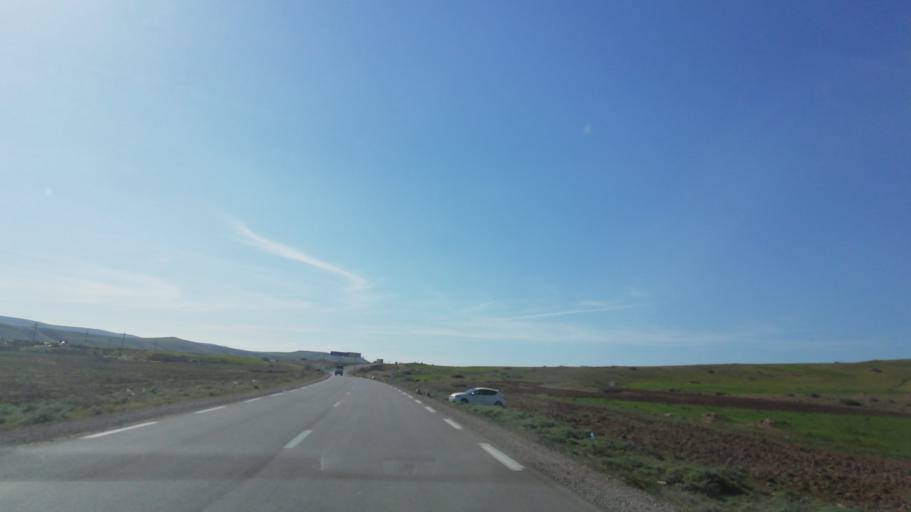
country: DZ
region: Mascara
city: Oued el Abtal
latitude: 35.4448
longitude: 0.8327
